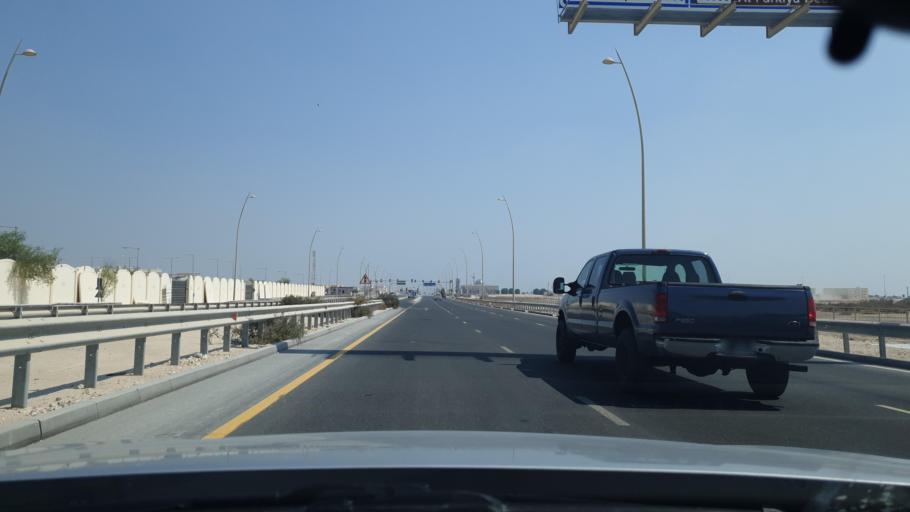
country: QA
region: Al Khawr
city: Al Khawr
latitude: 25.6614
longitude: 51.4894
